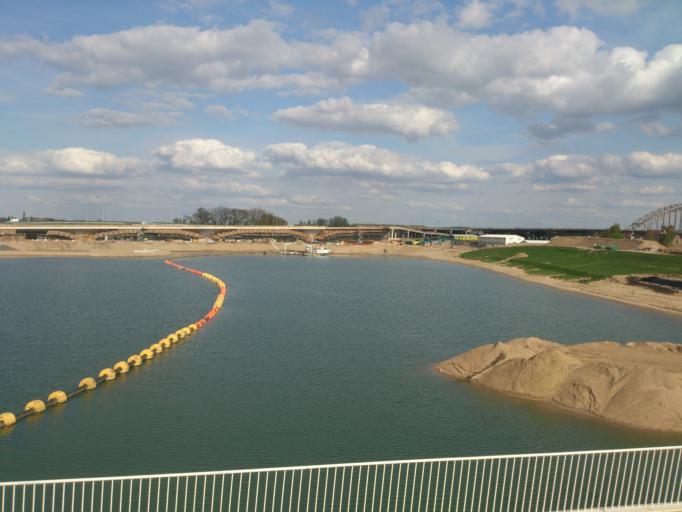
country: NL
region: Gelderland
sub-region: Gemeente Nijmegen
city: Nijmegen
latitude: 51.8559
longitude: 5.8620
